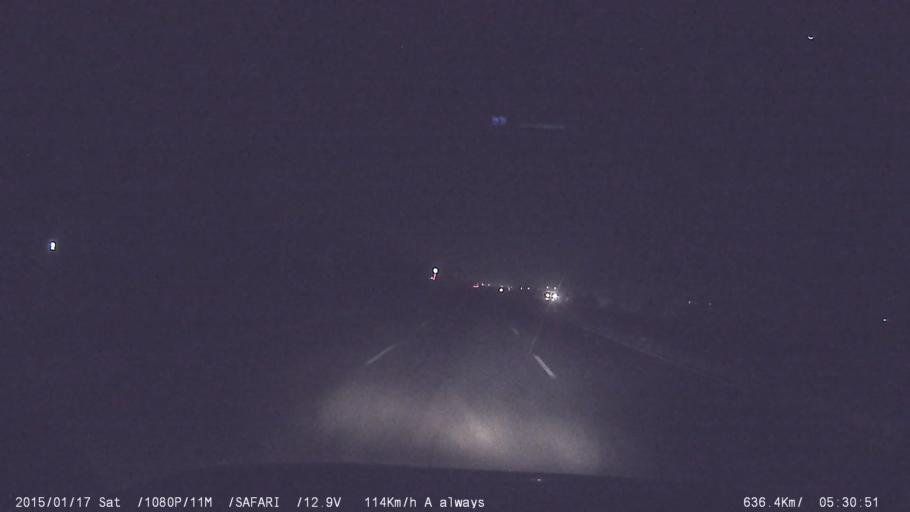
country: IN
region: Tamil Nadu
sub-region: Vellore
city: Arcot
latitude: 12.9125
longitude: 79.3065
